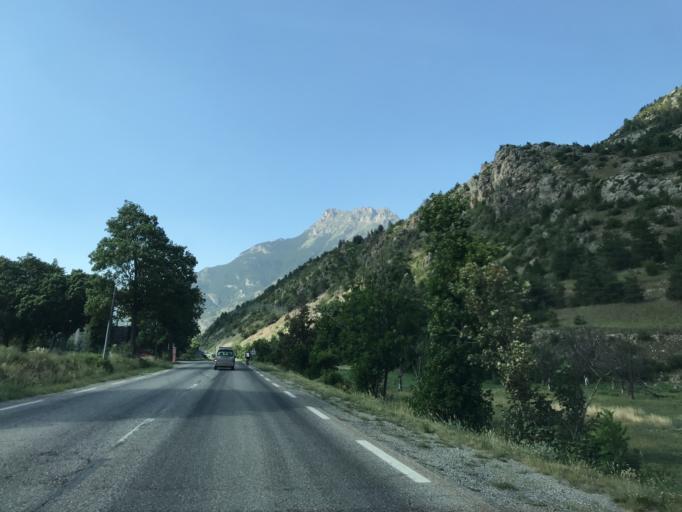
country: FR
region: Provence-Alpes-Cote d'Azur
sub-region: Departement des Hautes-Alpes
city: Saint-Martin-de-Queyrieres
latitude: 44.7364
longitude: 6.5839
